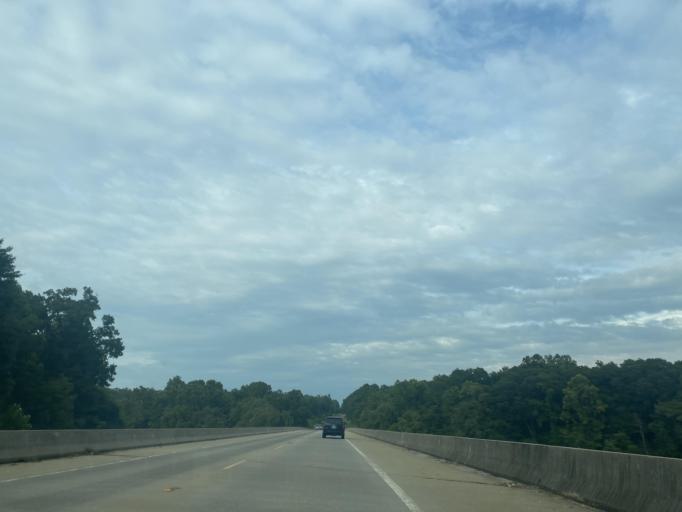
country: US
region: South Carolina
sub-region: Cherokee County
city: East Gaffney
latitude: 35.0885
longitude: -81.5734
